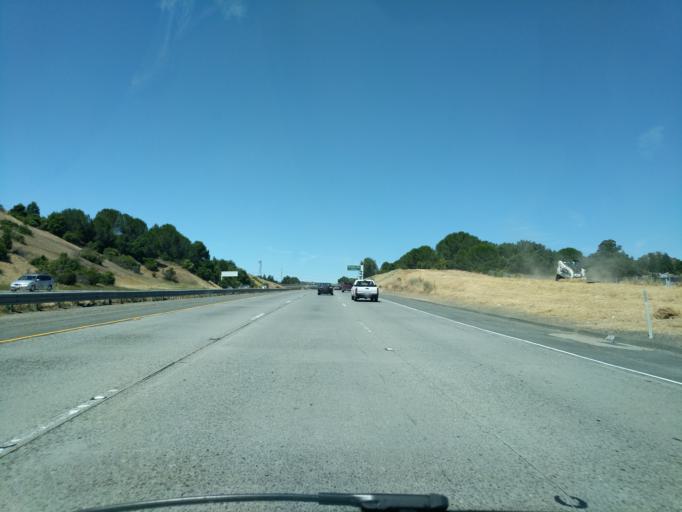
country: US
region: California
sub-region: Contra Costa County
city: Pacheco
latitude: 37.9918
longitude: -122.0798
